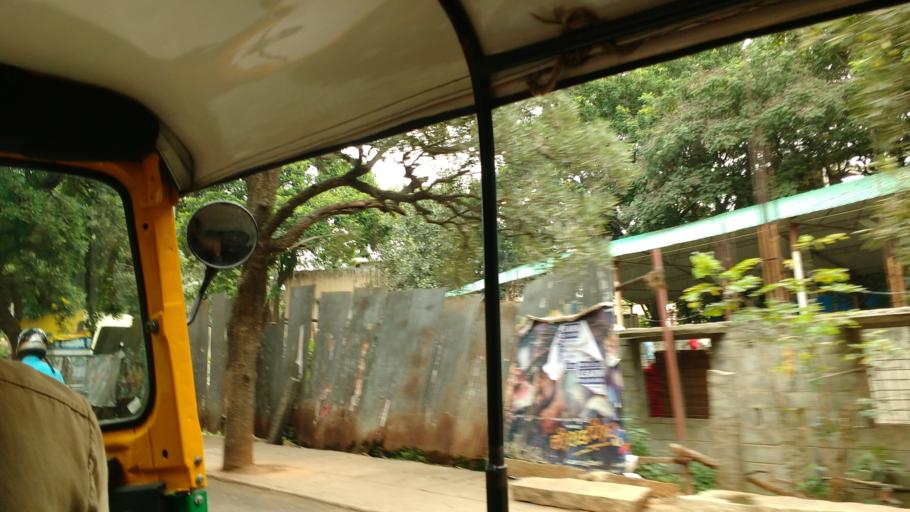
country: IN
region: Karnataka
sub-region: Bangalore Urban
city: Bangalore
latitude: 12.9742
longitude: 77.5383
